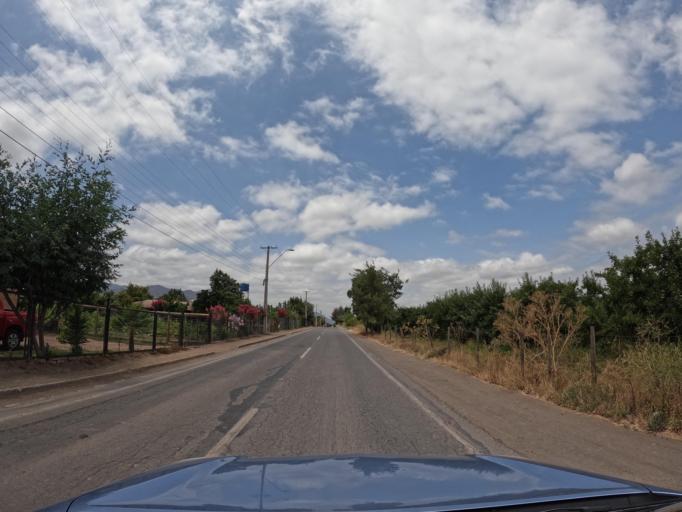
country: CL
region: O'Higgins
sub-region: Provincia de Colchagua
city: Chimbarongo
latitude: -34.7505
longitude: -70.9536
